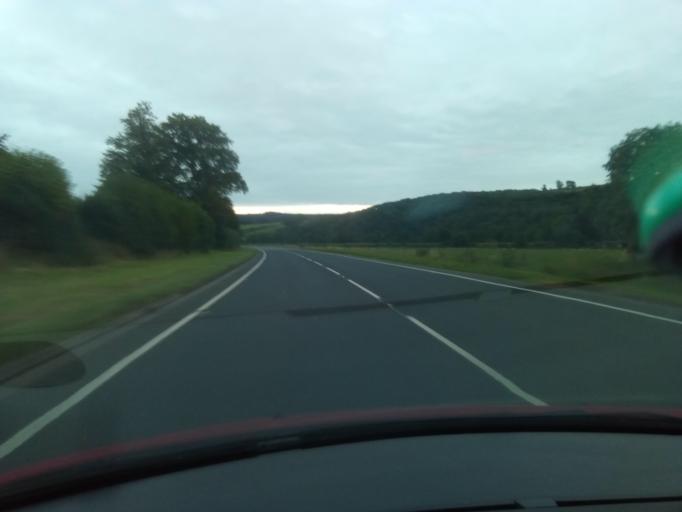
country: GB
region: England
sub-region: Northumberland
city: Bardon Mill
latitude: 54.9719
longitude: -2.2894
